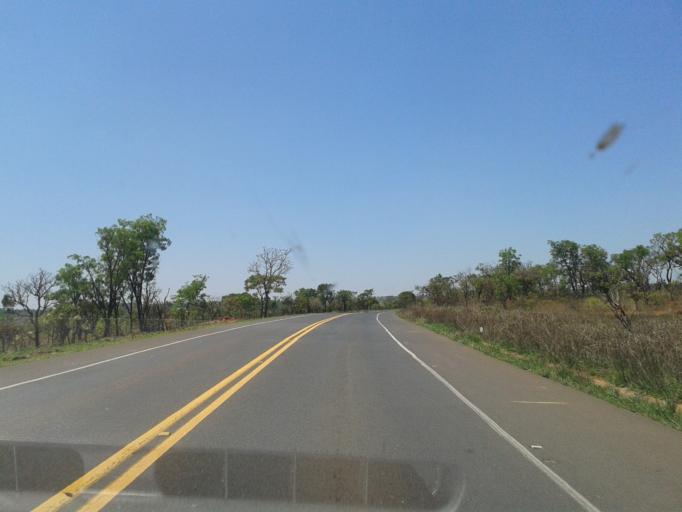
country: BR
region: Minas Gerais
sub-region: Araxa
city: Araxa
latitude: -19.4778
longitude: -47.1461
